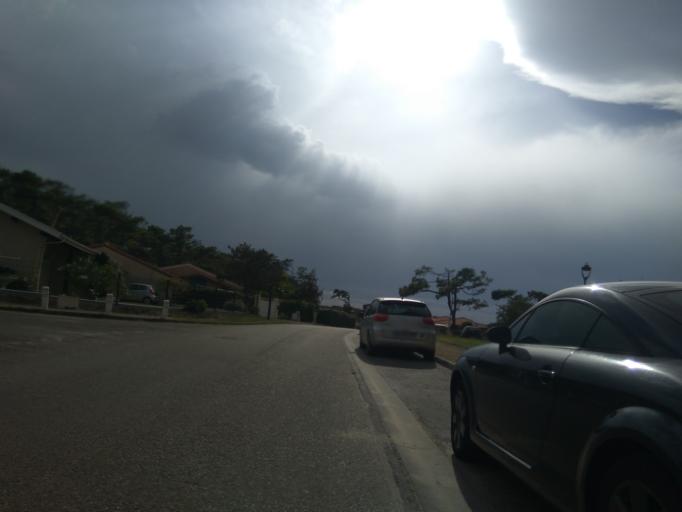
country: FR
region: Aquitaine
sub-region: Departement des Landes
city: Capbreton
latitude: 43.6339
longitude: -1.4456
